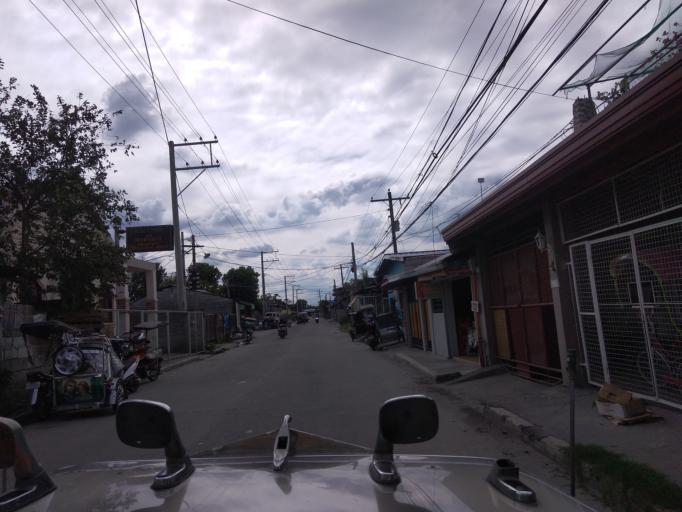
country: PH
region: Central Luzon
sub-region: Province of Pampanga
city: Pandacaqui
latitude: 15.1835
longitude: 120.6428
